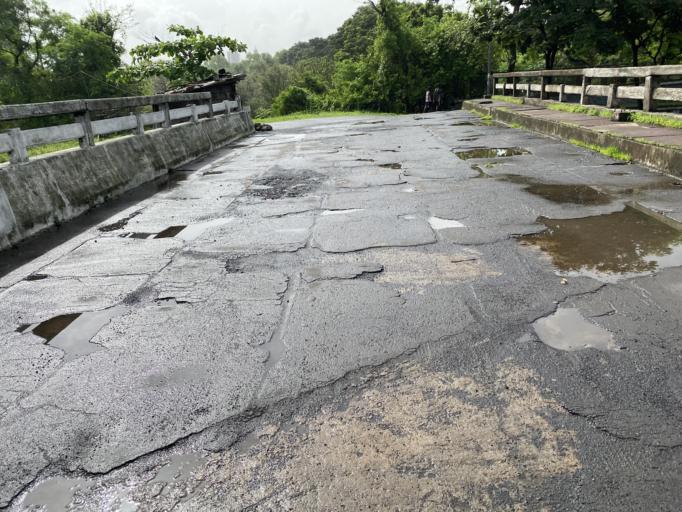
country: IN
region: Maharashtra
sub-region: Mumbai Suburban
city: Borivli
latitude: 19.2618
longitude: 72.8546
